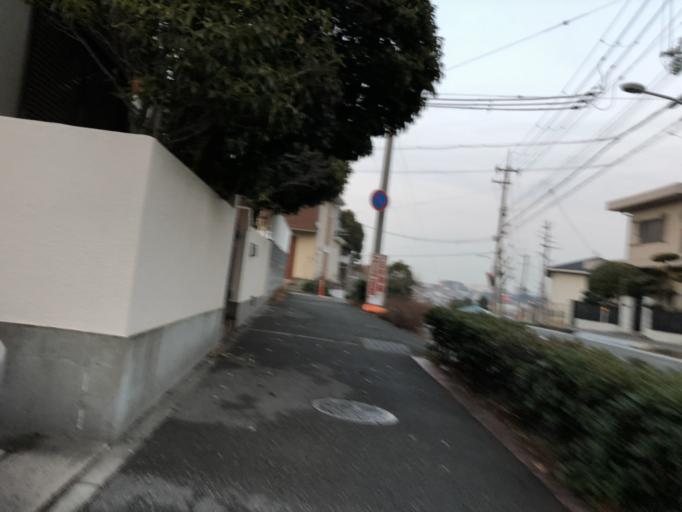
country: JP
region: Hyogo
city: Akashi
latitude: 34.6505
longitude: 135.0187
